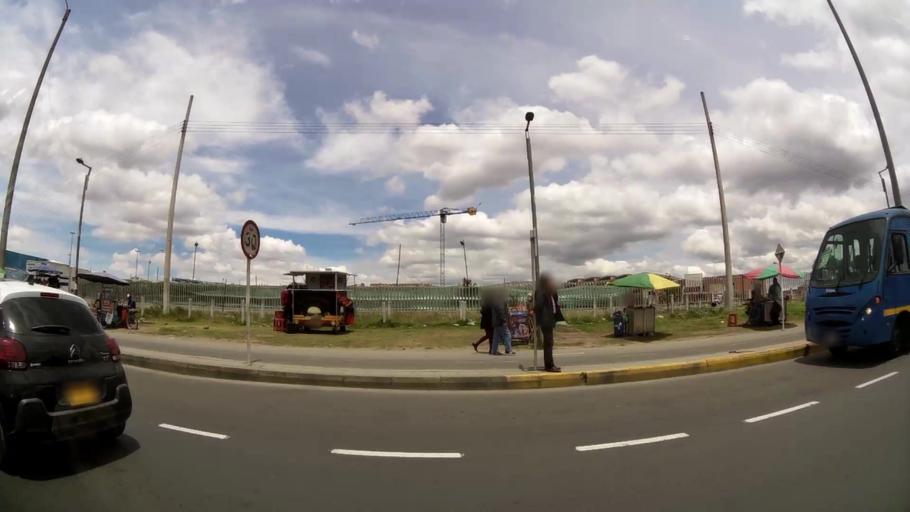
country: CO
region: Bogota D.C.
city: Bogota
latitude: 4.6519
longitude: -74.1443
